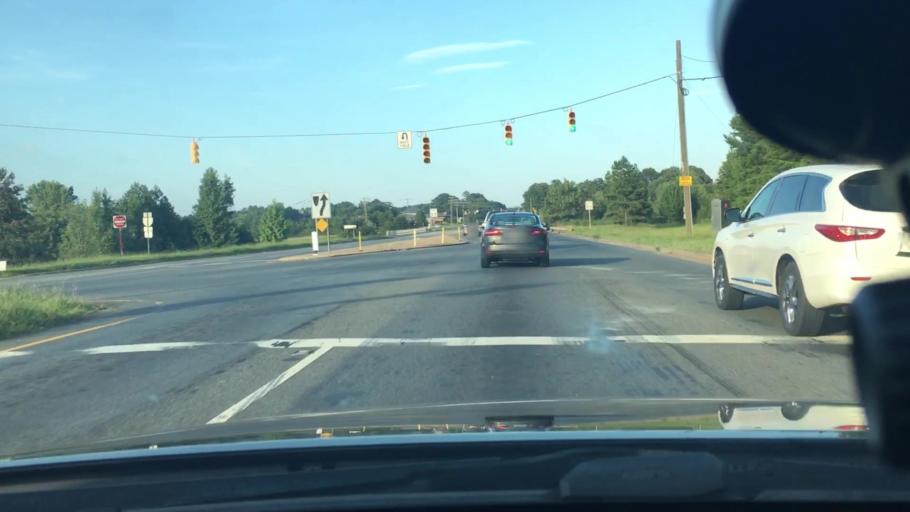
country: US
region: North Carolina
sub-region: Mecklenburg County
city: Mint Hill
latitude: 35.2190
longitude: -80.6512
